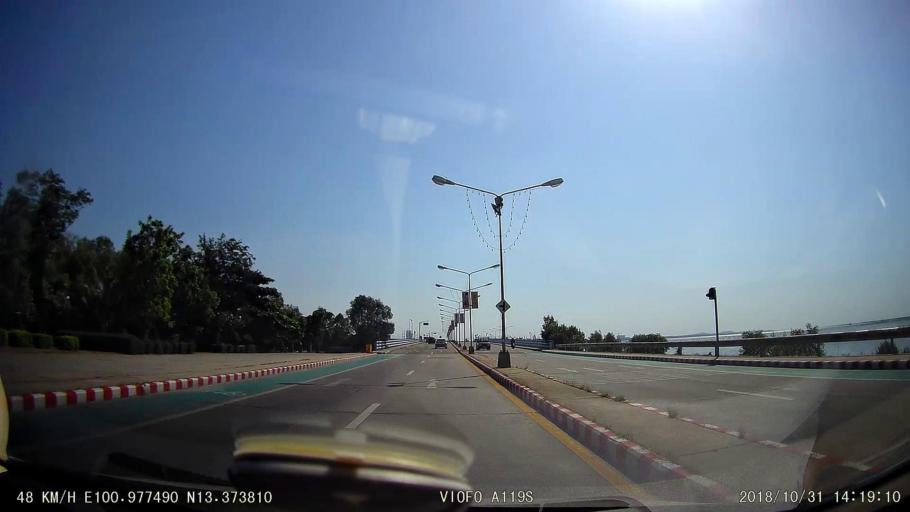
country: TH
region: Chon Buri
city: Chon Buri
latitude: 13.3738
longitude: 100.9775
